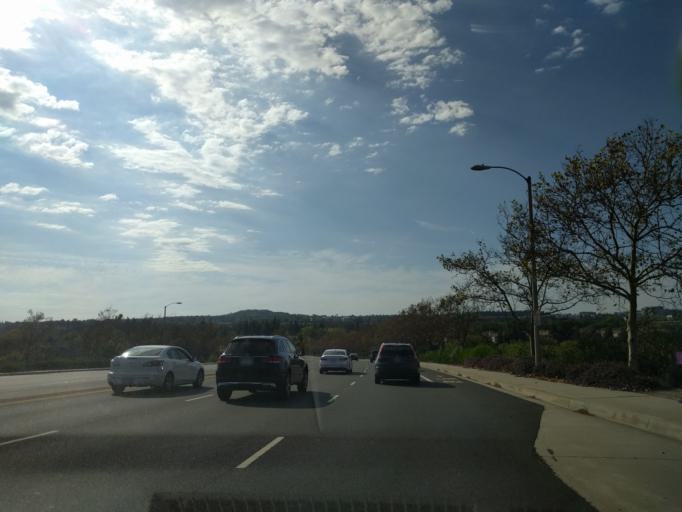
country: US
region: California
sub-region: Orange County
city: Aliso Viejo
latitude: 33.5717
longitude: -117.7148
